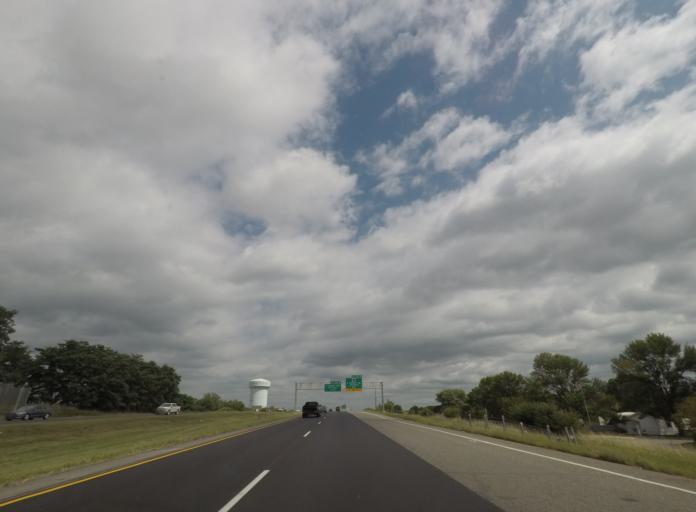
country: US
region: Iowa
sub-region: Linn County
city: Cedar Rapids
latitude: 41.9267
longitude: -91.6503
